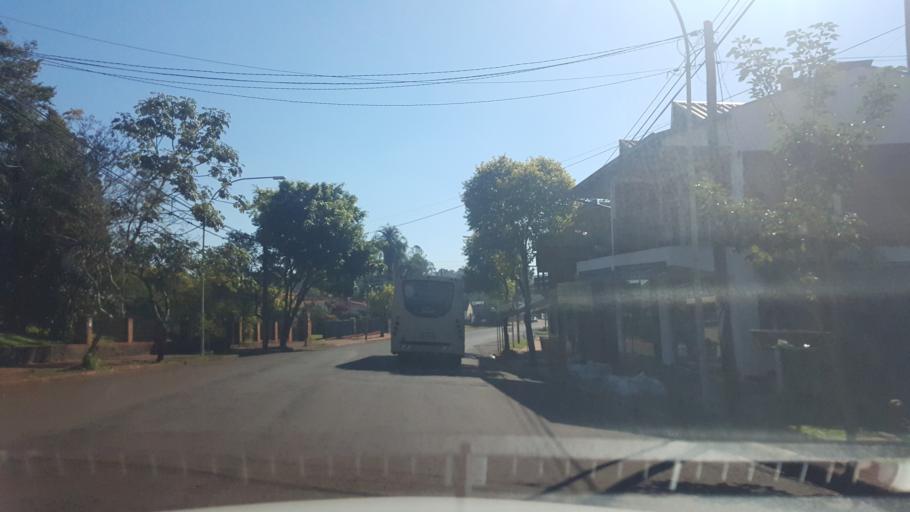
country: AR
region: Misiones
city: Puerto Rico
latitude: -26.8018
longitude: -55.0209
